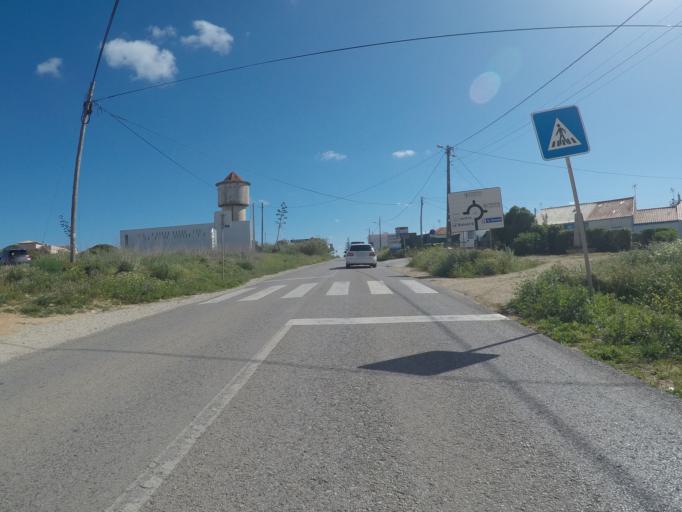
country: PT
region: Faro
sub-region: Vila do Bispo
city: Sagres
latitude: 37.0098
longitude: -8.9439
